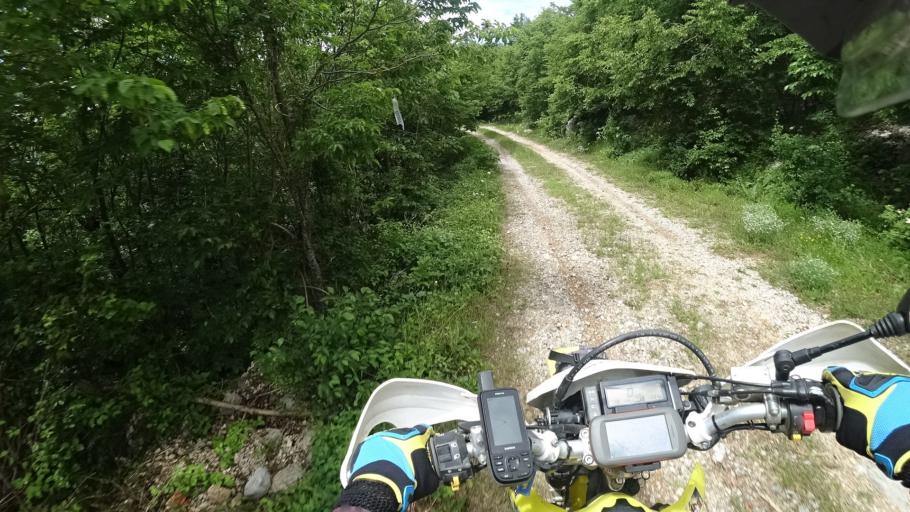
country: HR
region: Primorsko-Goranska
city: Bribir
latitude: 45.2032
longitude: 14.7617
